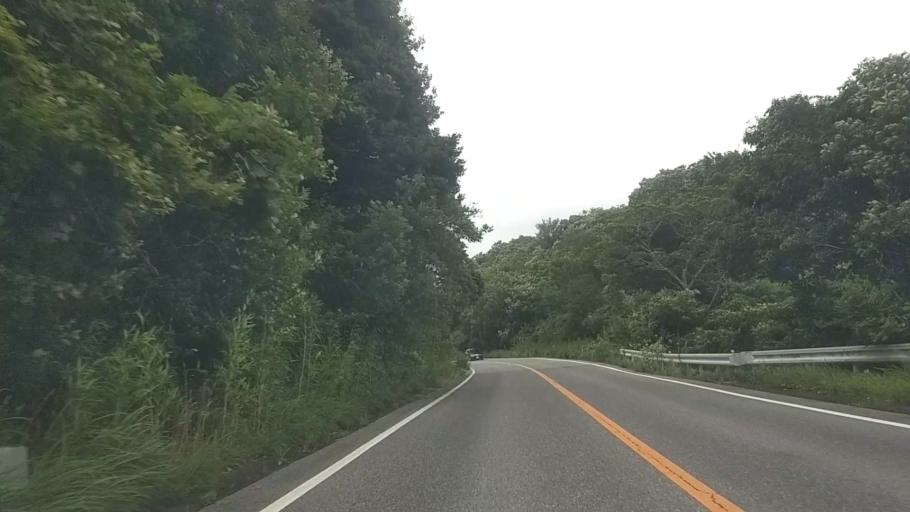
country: JP
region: Chiba
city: Kimitsu
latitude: 35.2400
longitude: 140.0065
